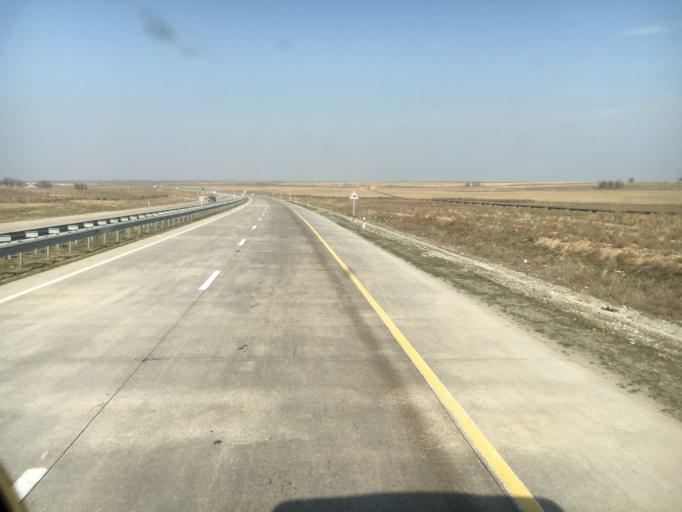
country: KZ
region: Ongtustik Qazaqstan
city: Shymkent
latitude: 42.4839
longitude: 69.5261
